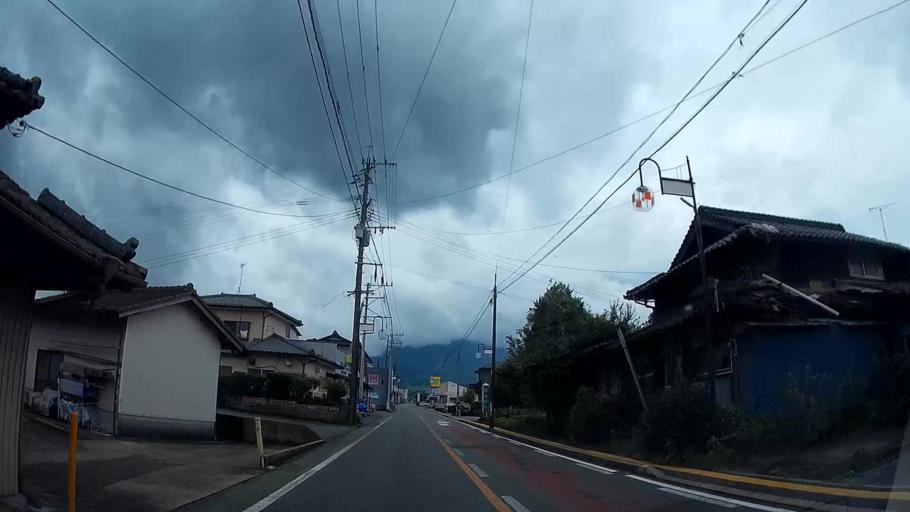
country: JP
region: Kumamoto
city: Aso
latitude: 32.9459
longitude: 131.1179
